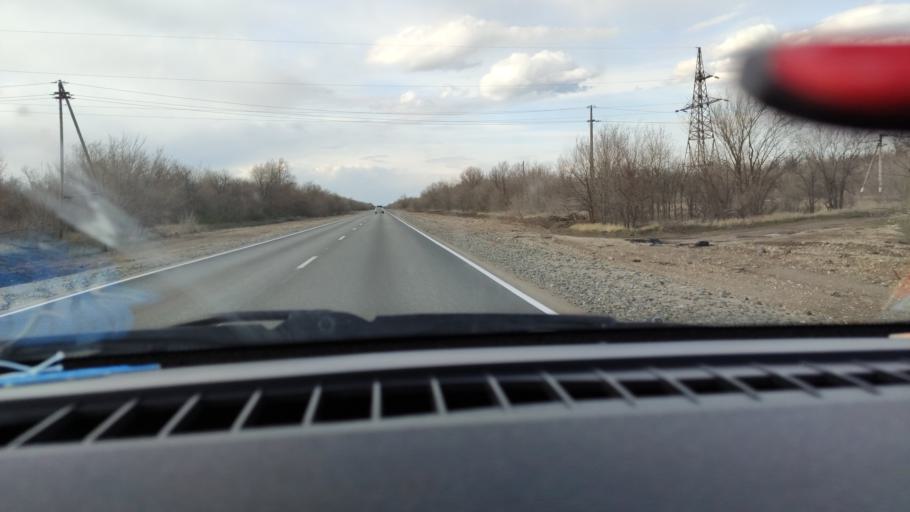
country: RU
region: Saratov
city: Privolzhskiy
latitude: 51.1373
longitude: 45.9601
